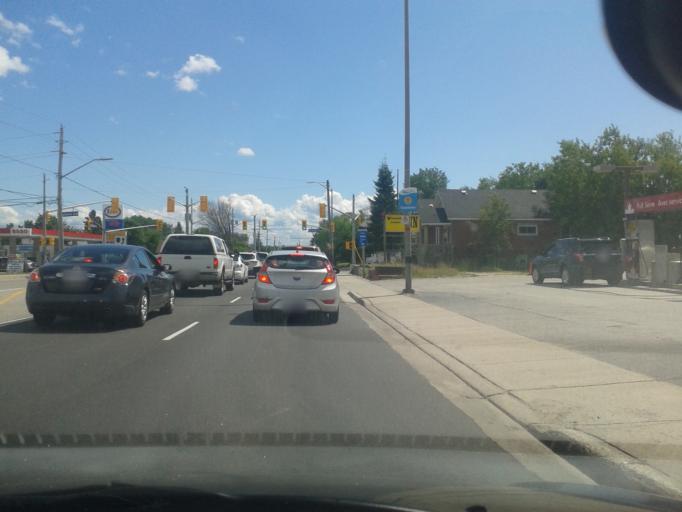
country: CA
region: Ontario
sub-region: Nipissing District
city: North Bay
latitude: 46.3263
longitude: -79.4663
